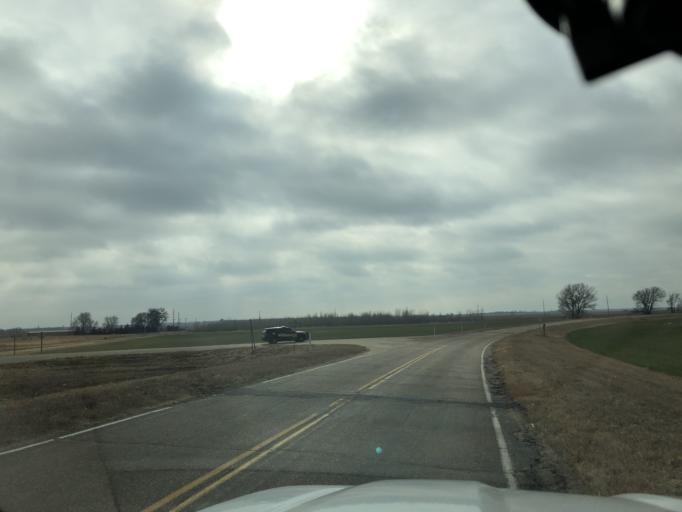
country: US
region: Kansas
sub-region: Stafford County
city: Stafford
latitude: 37.9590
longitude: -98.3998
